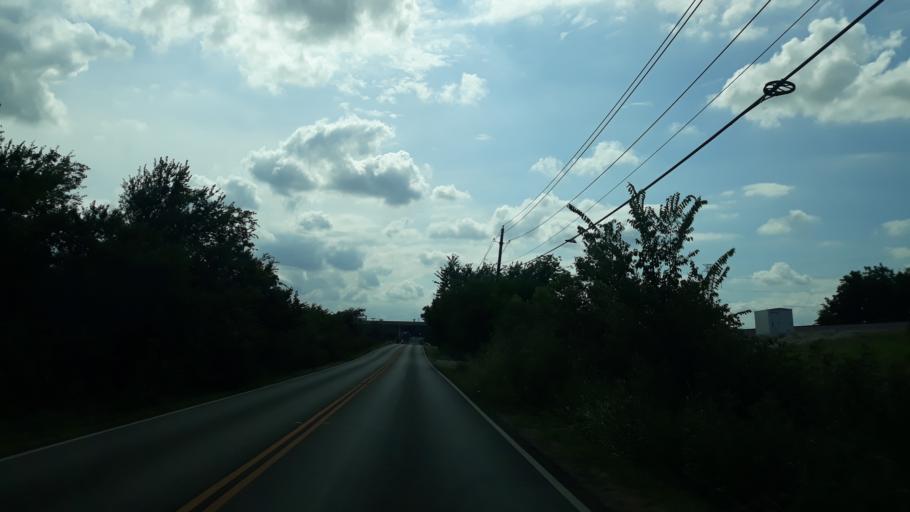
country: US
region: Texas
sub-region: Dallas County
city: Irving
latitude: 32.8158
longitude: -97.0121
